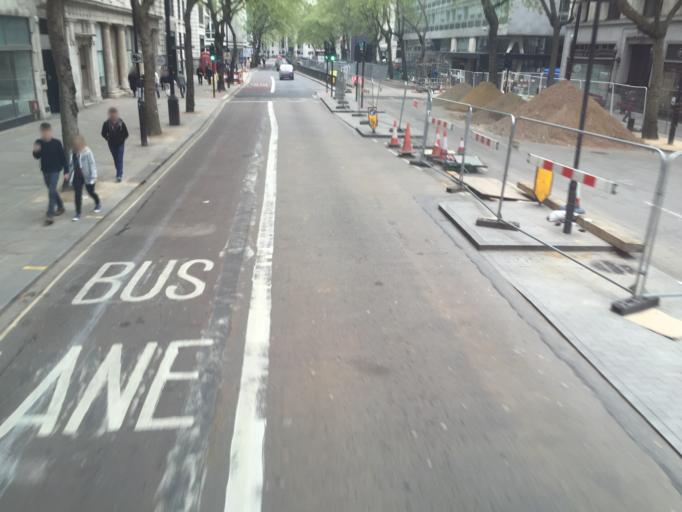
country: GB
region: England
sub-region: Greater London
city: London
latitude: 51.5158
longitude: -0.1192
